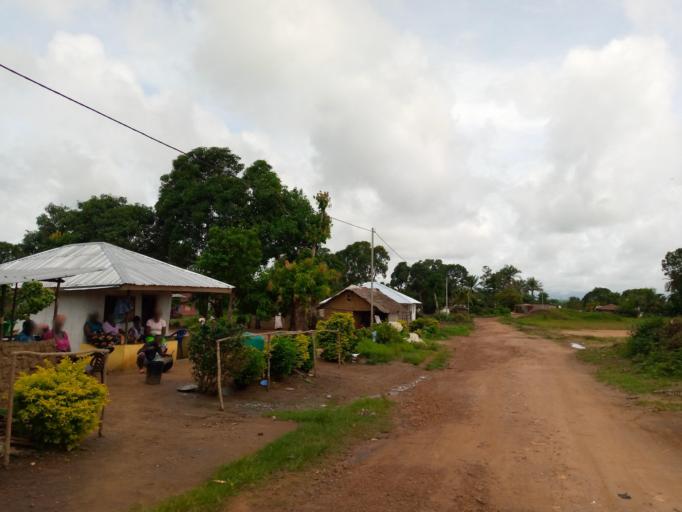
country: SL
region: Southern Province
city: Mogbwemo
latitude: 7.7640
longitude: -12.3103
